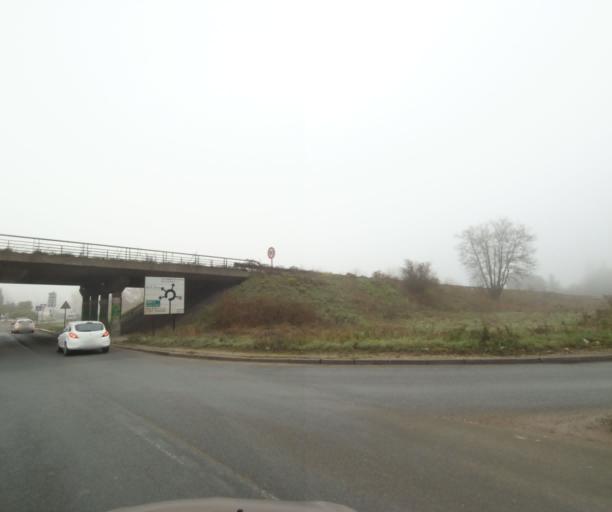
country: FR
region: Ile-de-France
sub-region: Departement de Seine-et-Marne
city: Villeparisis
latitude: 48.9343
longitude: 2.6022
